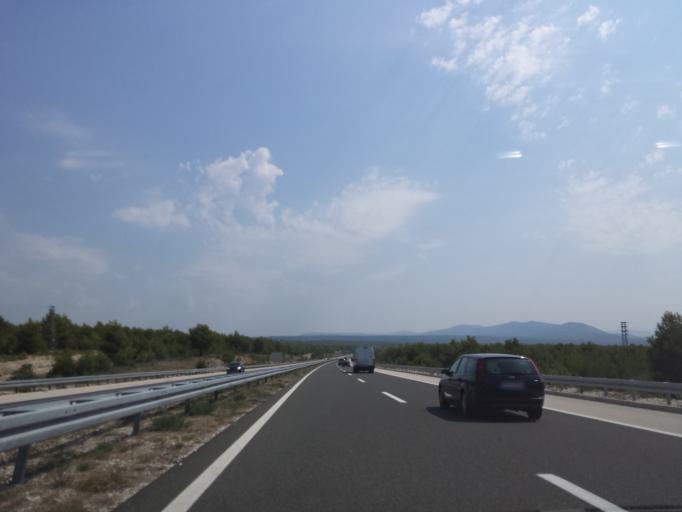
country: HR
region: Sibensko-Kniniska
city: Zaton
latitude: 43.8471
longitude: 15.8707
